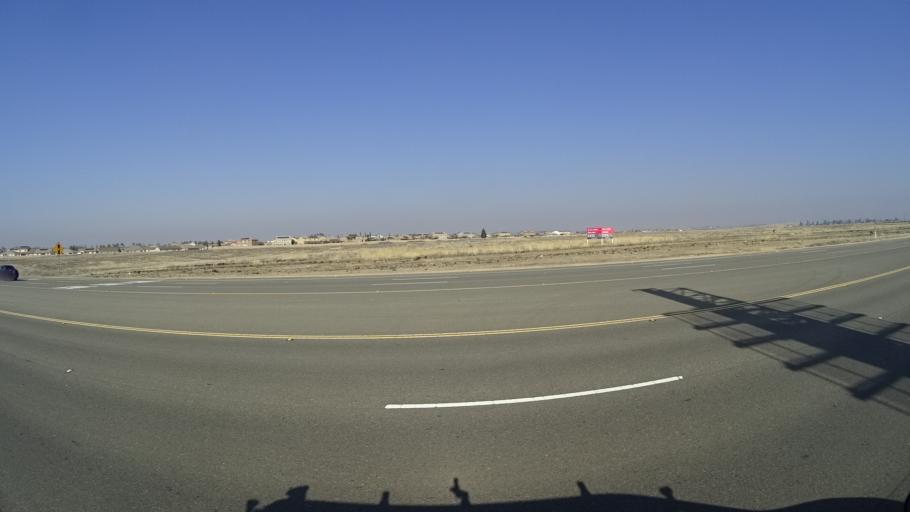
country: US
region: California
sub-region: Kern County
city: Bakersfield
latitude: 35.3980
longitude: -118.8858
